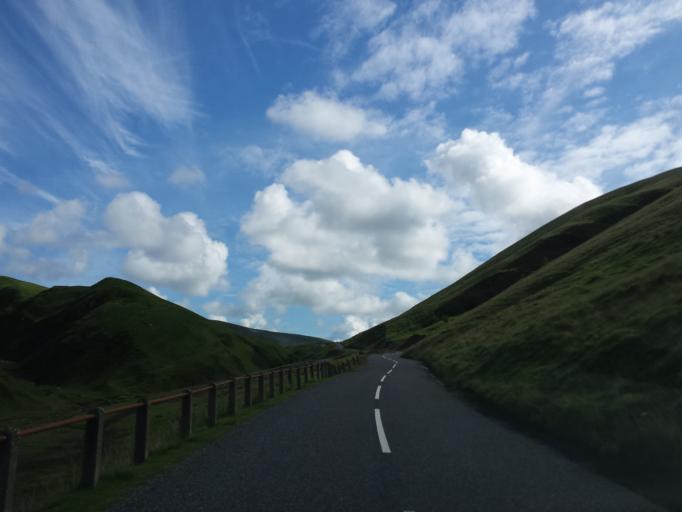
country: GB
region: Scotland
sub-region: Dumfries and Galloway
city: Moffat
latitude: 55.4247
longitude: -3.2737
